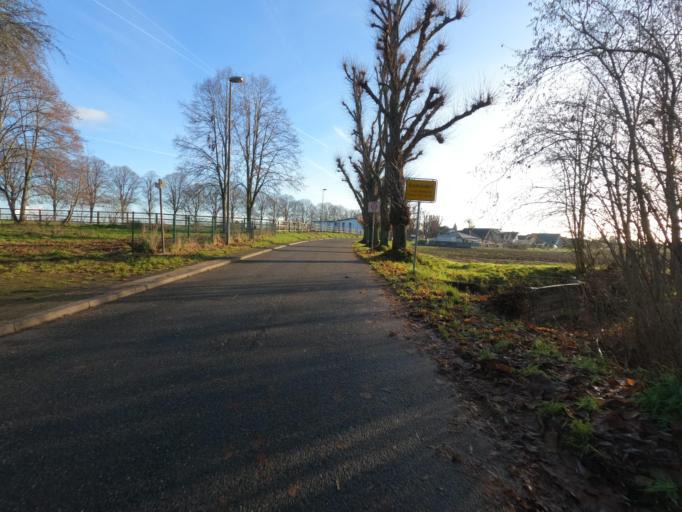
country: DE
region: North Rhine-Westphalia
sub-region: Regierungsbezirk Koln
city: Bedburg
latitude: 50.9863
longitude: 6.5089
